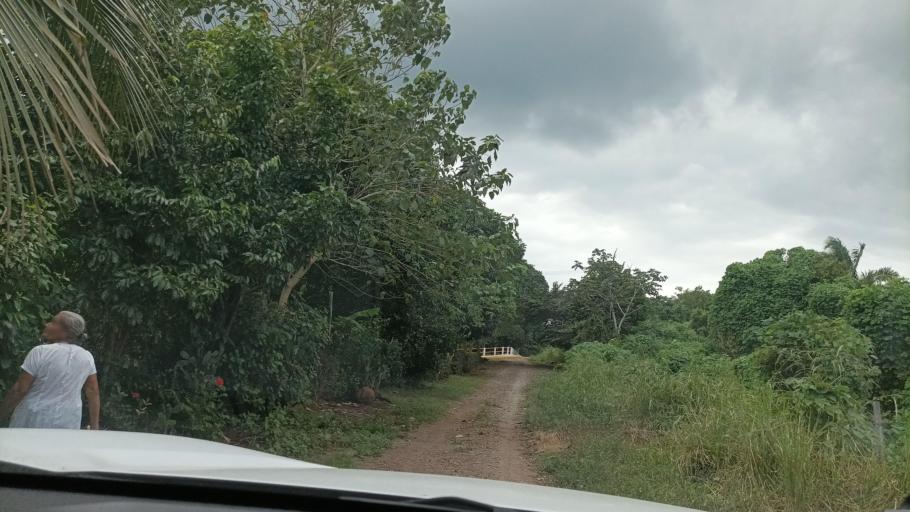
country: MX
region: Veracruz
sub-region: Pajapan
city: Pajapan
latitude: 18.1858
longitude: -94.6715
